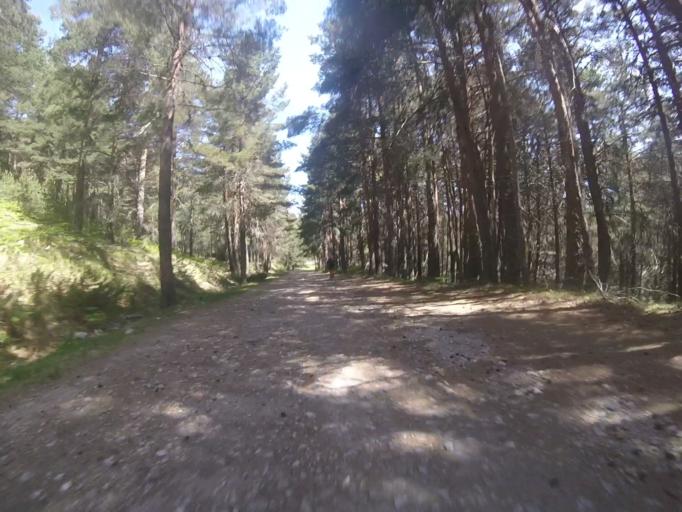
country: ES
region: Madrid
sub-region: Provincia de Madrid
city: Cercedilla
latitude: 40.8112
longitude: -4.0565
